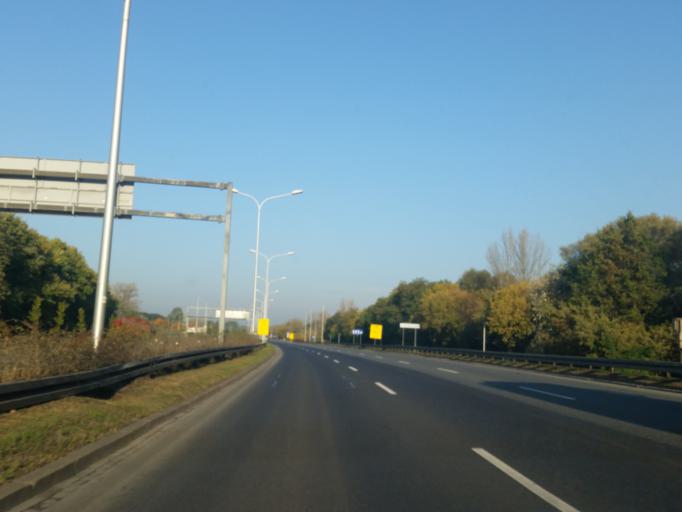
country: PL
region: Masovian Voivodeship
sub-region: Warszawa
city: Zoliborz
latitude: 52.2889
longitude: 20.9811
